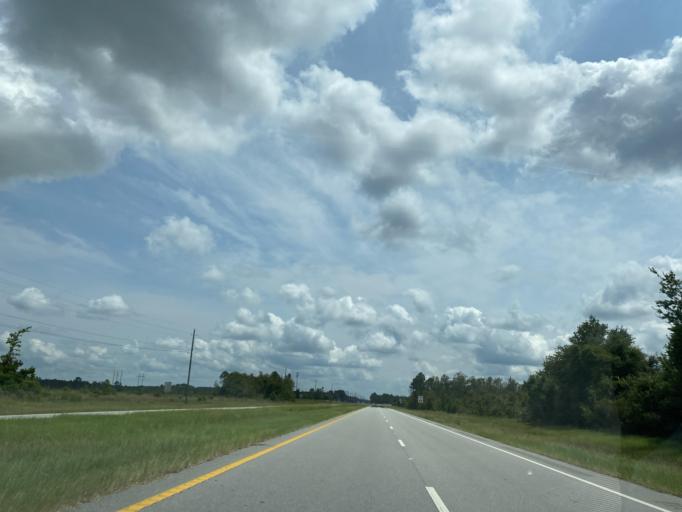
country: US
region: Georgia
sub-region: Ware County
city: Deenwood
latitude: 31.2551
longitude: -82.4301
